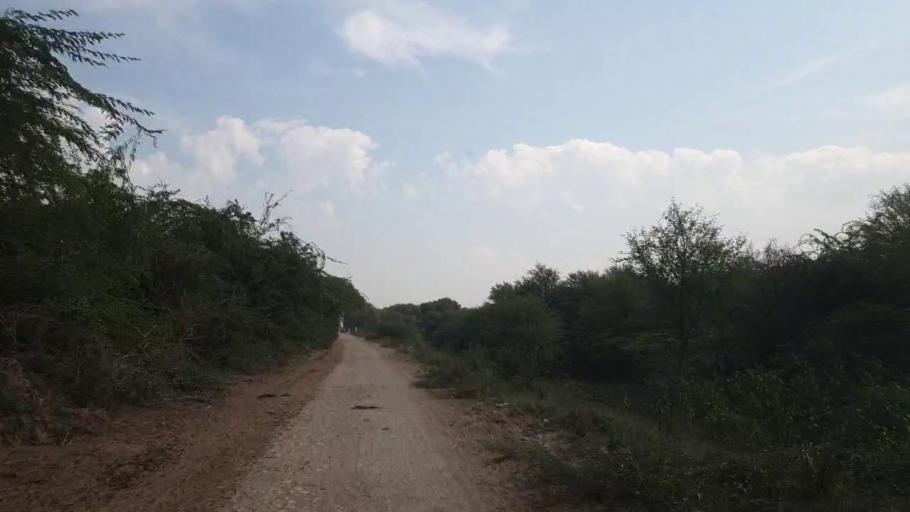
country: PK
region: Sindh
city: Tando Bago
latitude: 24.9258
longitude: 69.0162
